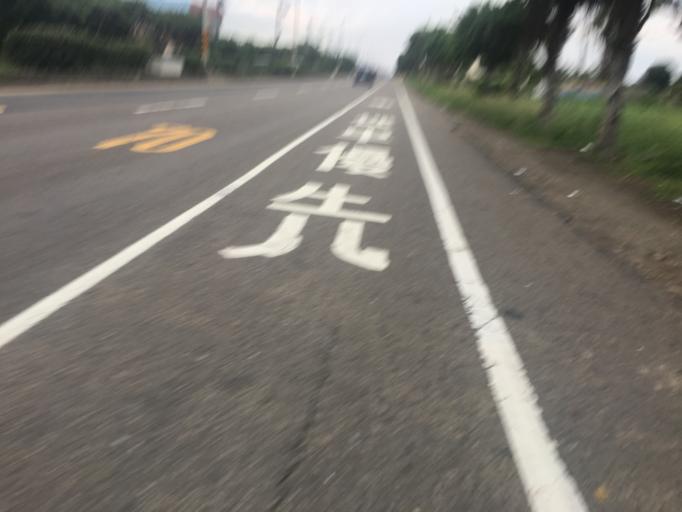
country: TW
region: Taiwan
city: Taoyuan City
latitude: 25.0883
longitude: 121.2267
